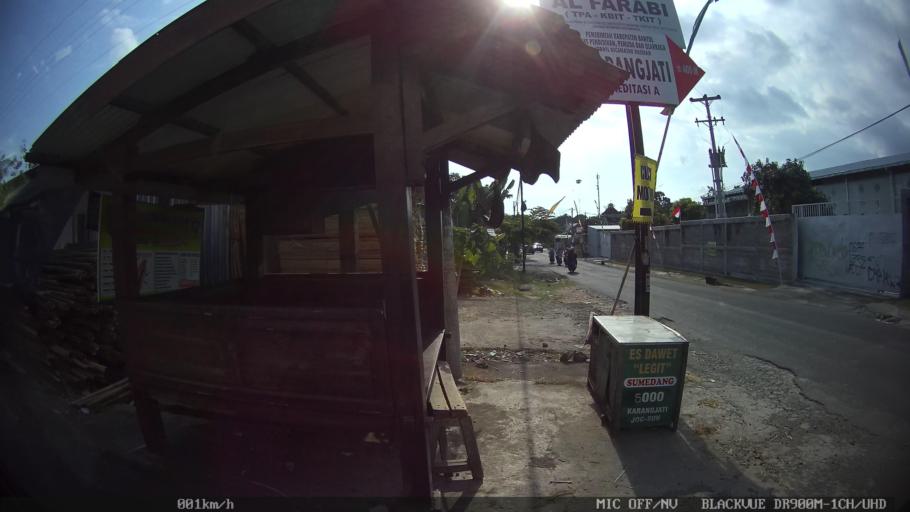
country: ID
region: Daerah Istimewa Yogyakarta
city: Kasihan
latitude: -7.8381
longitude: 110.3182
